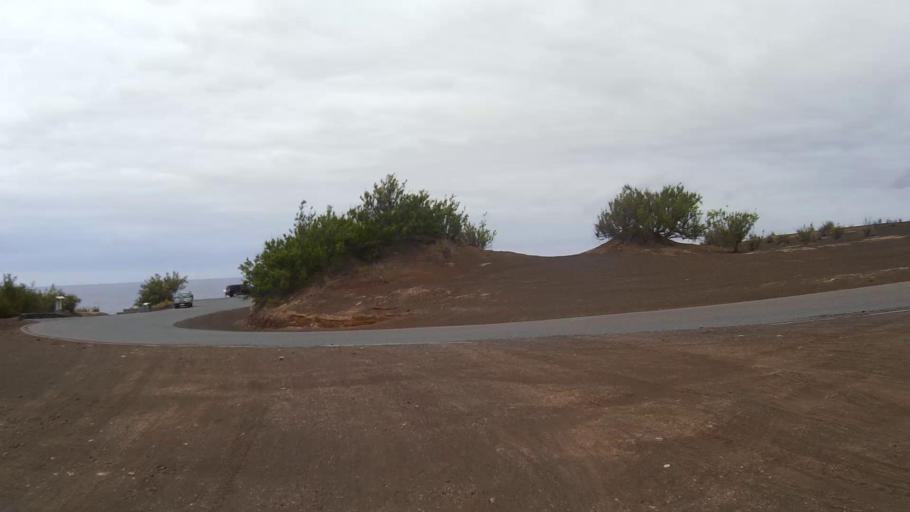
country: PT
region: Azores
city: Ribeira Grande
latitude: 38.5930
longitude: -28.8259
